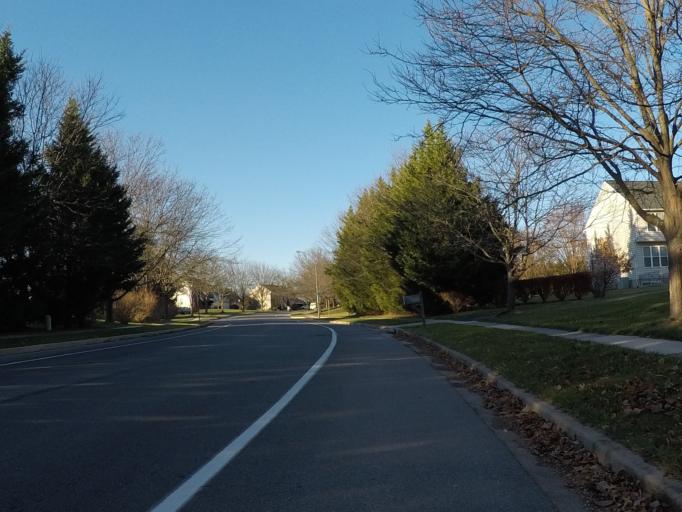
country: US
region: Maryland
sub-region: Howard County
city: Columbia
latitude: 39.2629
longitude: -76.8441
